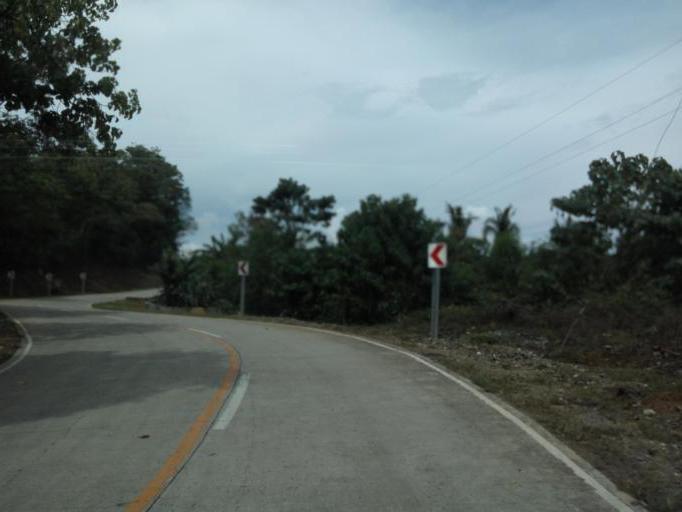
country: PH
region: Cagayan Valley
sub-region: Province of Quirino
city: Dumabato
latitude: 16.2590
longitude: 121.6765
